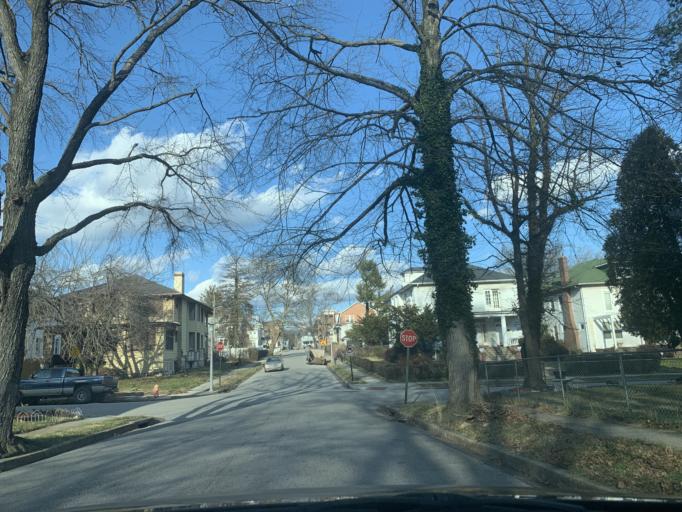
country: US
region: Maryland
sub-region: Baltimore County
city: Lochearn
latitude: 39.3226
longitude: -76.6742
